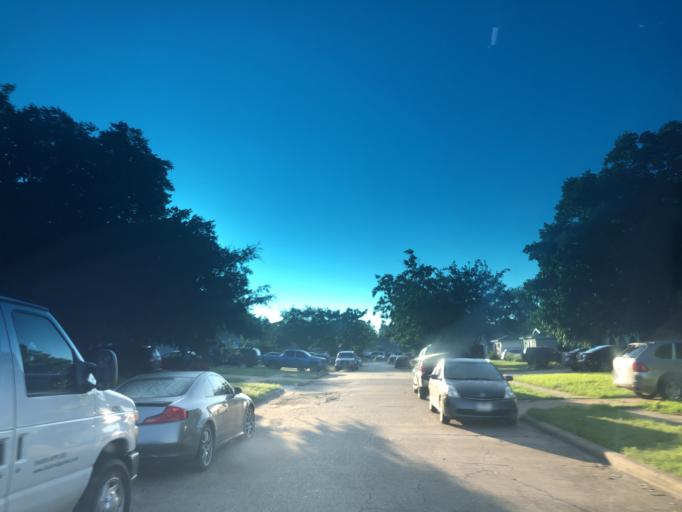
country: US
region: Texas
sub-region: Dallas County
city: Grand Prairie
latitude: 32.7058
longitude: -97.0153
